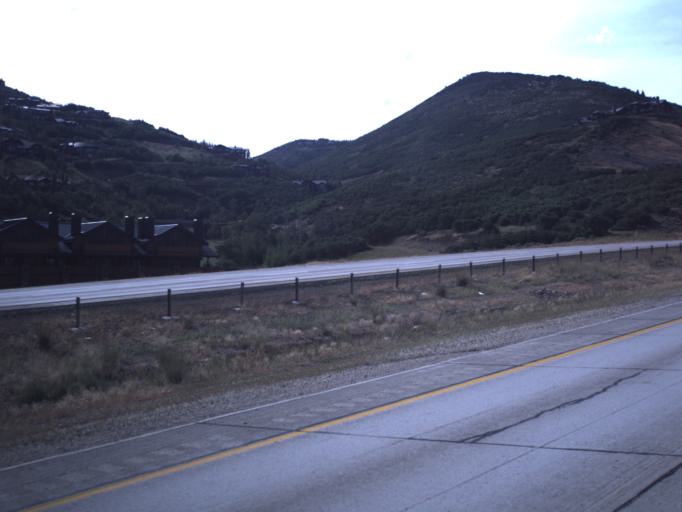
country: US
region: Utah
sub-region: Summit County
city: Park City
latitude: 40.6359
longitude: -111.4499
